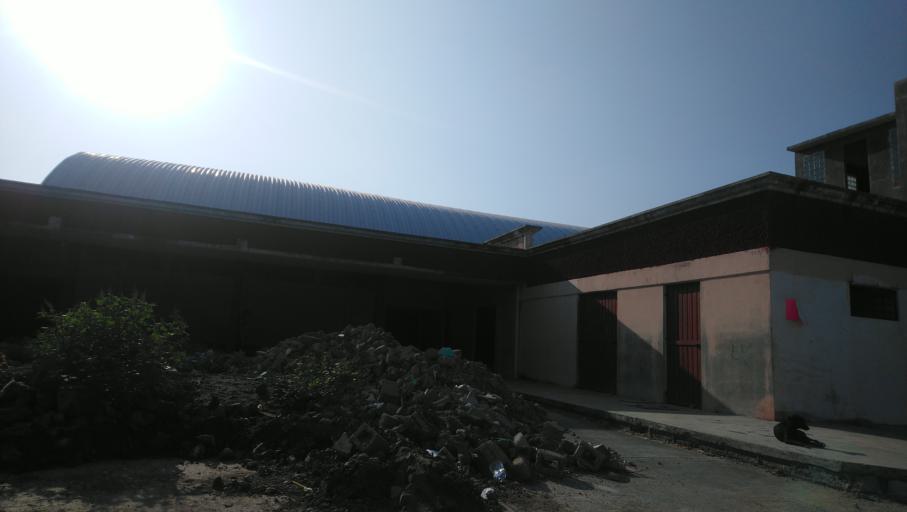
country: MX
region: Oaxaca
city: San Mateo del Mar
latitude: 16.2103
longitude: -94.9829
